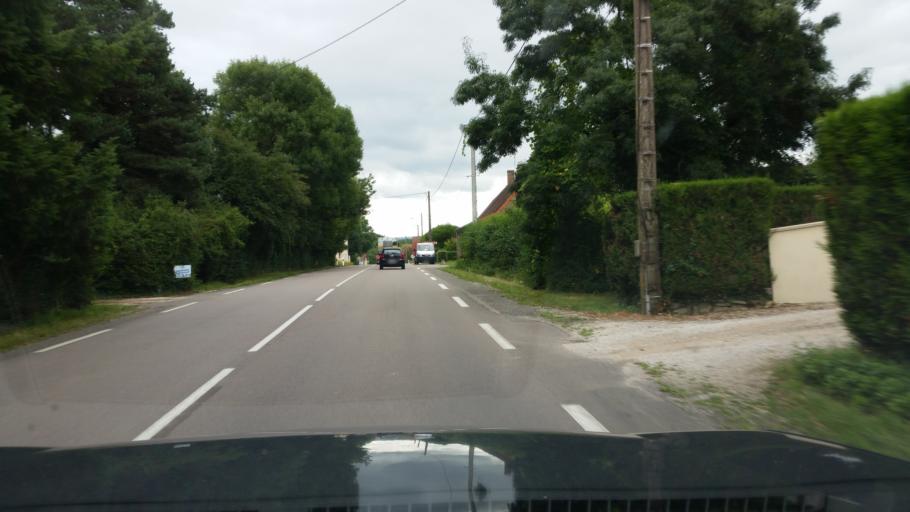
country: FR
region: Franche-Comte
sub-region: Departement du Jura
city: Bletterans
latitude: 46.6709
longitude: 5.3988
